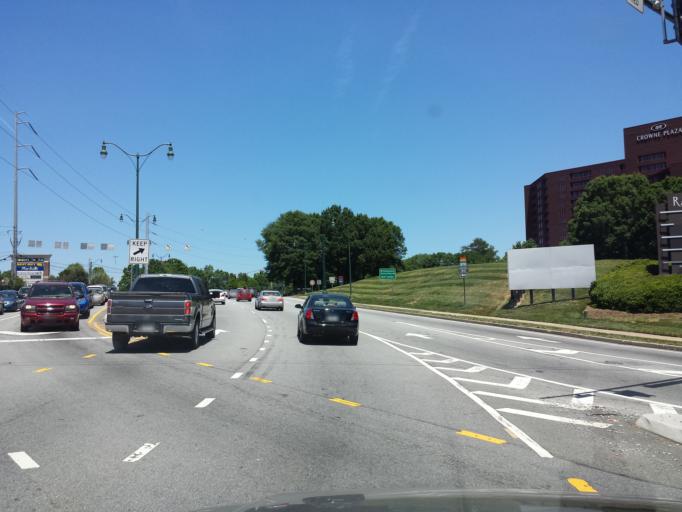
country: US
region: Georgia
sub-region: DeKalb County
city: Dunwoody
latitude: 33.9188
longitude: -84.3385
